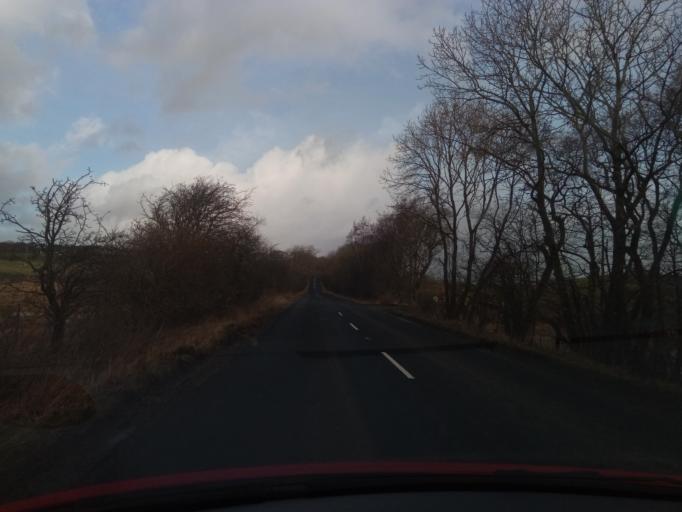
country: GB
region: England
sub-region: Northumberland
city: Acomb
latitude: 55.0965
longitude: -2.0492
